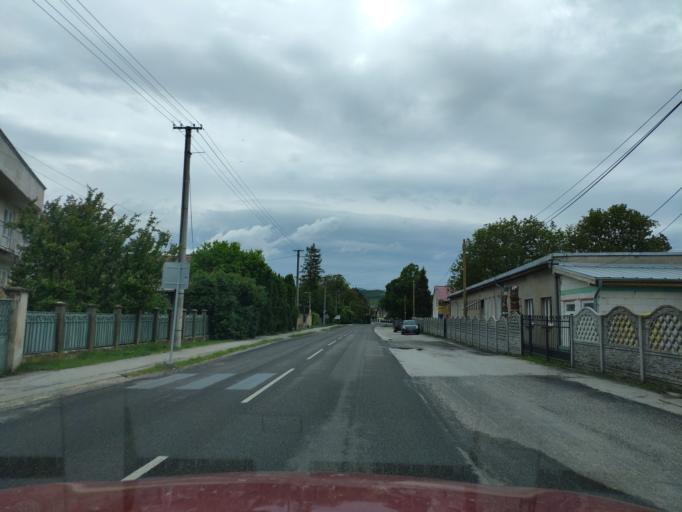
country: SK
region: Kosicky
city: Kosice
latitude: 48.7072
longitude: 21.3308
